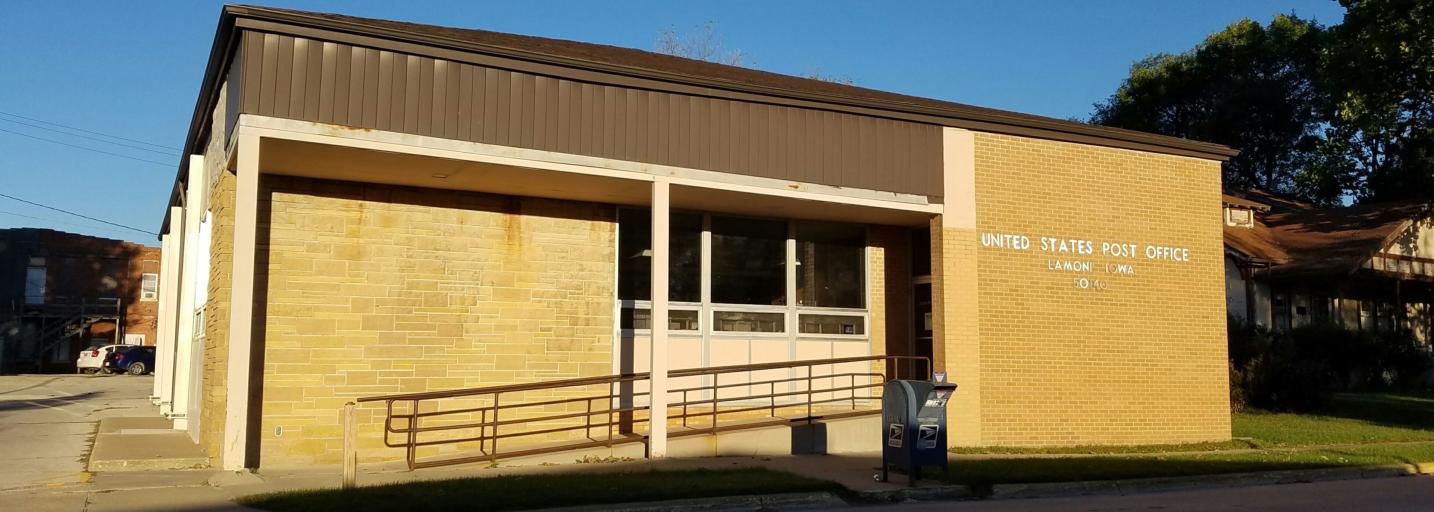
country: US
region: Iowa
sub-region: Decatur County
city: Lamoni
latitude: 40.6241
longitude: -93.9320
